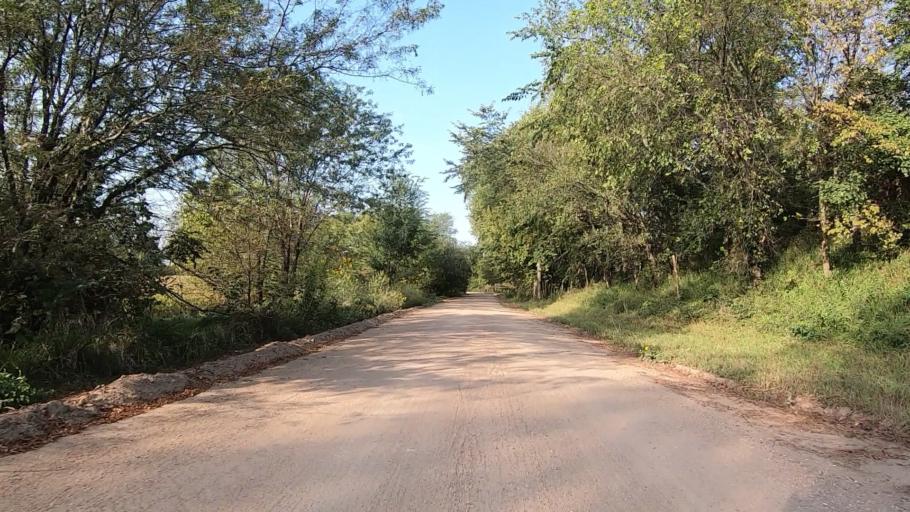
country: US
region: Kansas
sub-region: Marshall County
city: Blue Rapids
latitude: 39.6674
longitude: -96.8132
